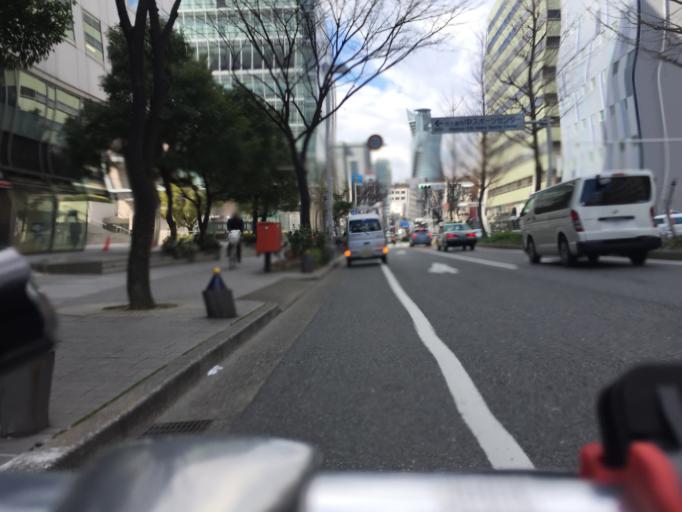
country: JP
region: Aichi
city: Nagoya-shi
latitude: 35.1679
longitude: 136.8944
